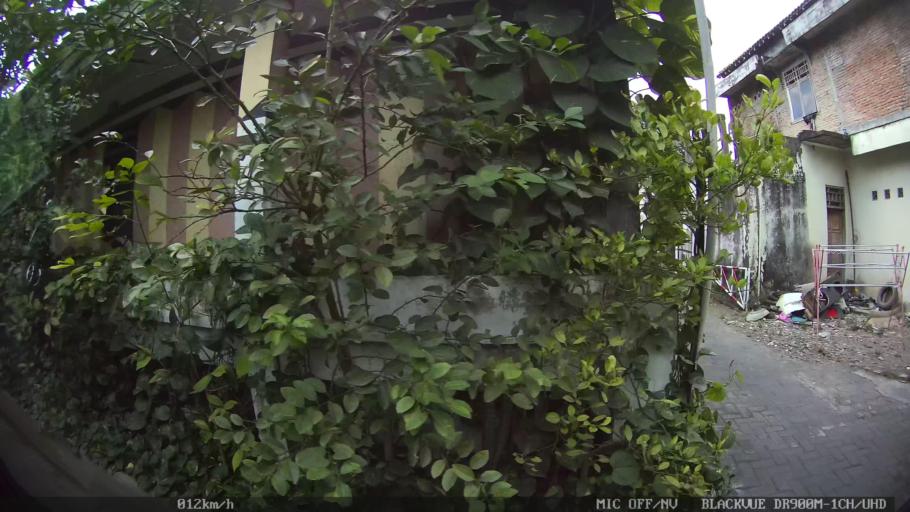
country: ID
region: Daerah Istimewa Yogyakarta
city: Yogyakarta
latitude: -7.8205
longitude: 110.4036
